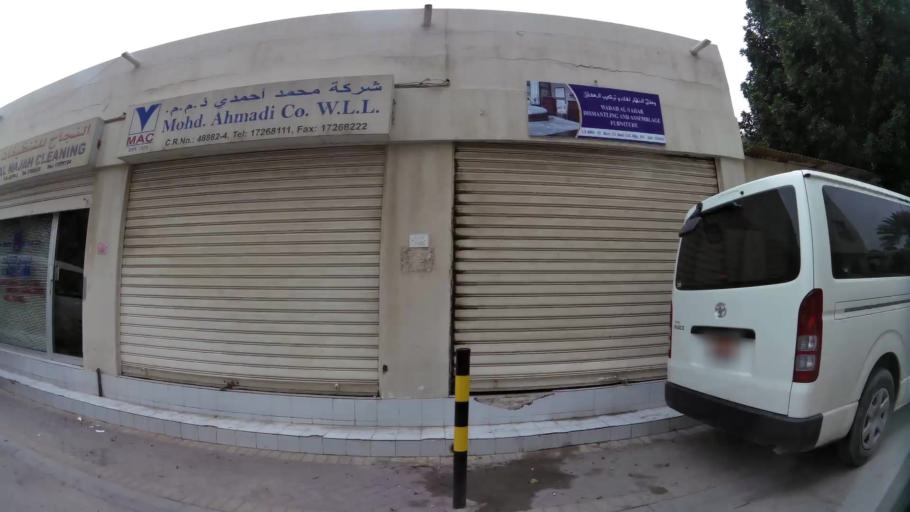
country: BH
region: Manama
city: Jidd Hafs
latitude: 26.2199
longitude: 50.5656
